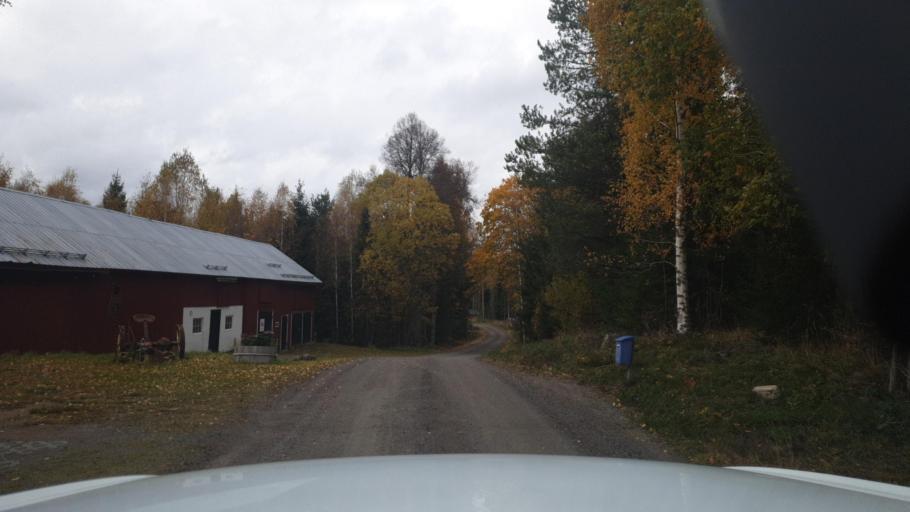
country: SE
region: Vaermland
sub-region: Torsby Kommun
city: Torsby
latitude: 59.9384
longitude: 12.8155
